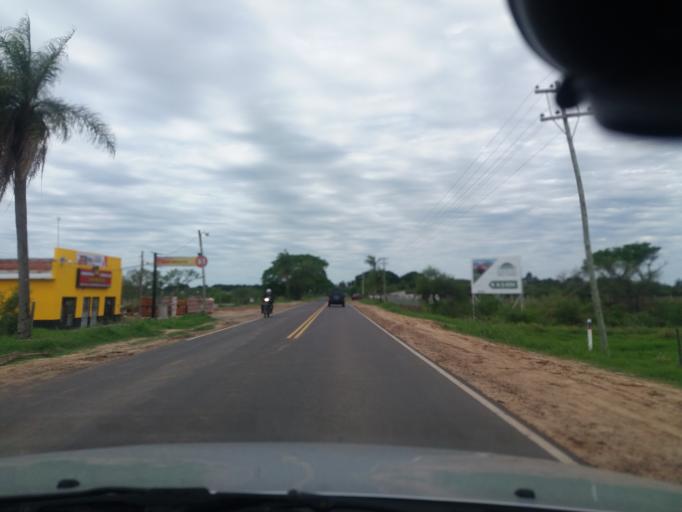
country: AR
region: Corrientes
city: Corrientes
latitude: -27.4494
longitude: -58.7451
